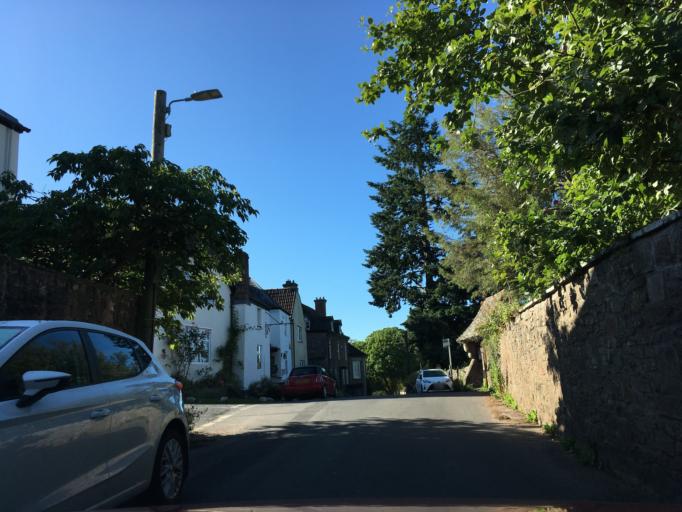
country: GB
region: England
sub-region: Gloucestershire
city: Coleford
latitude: 51.7834
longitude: -2.6489
